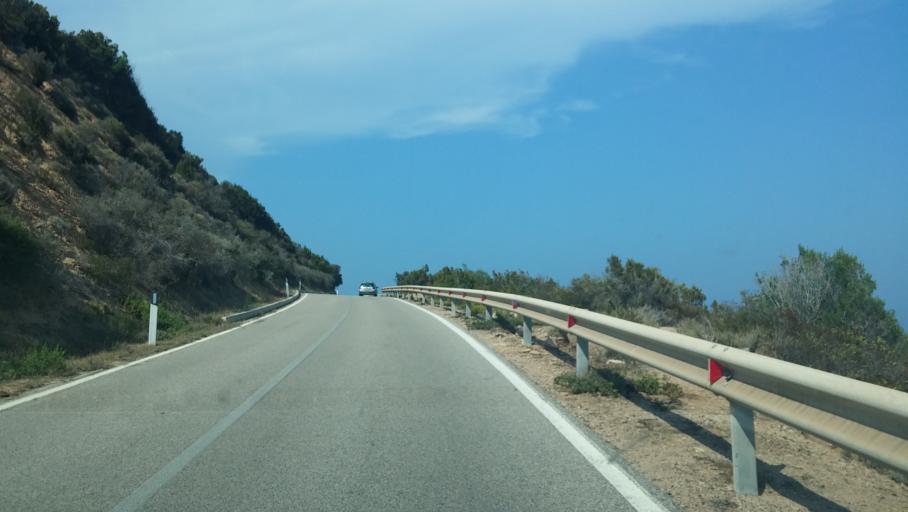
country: IT
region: Sardinia
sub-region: Provincia di Olbia-Tempio
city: La Maddalena
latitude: 41.2503
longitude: 9.4279
